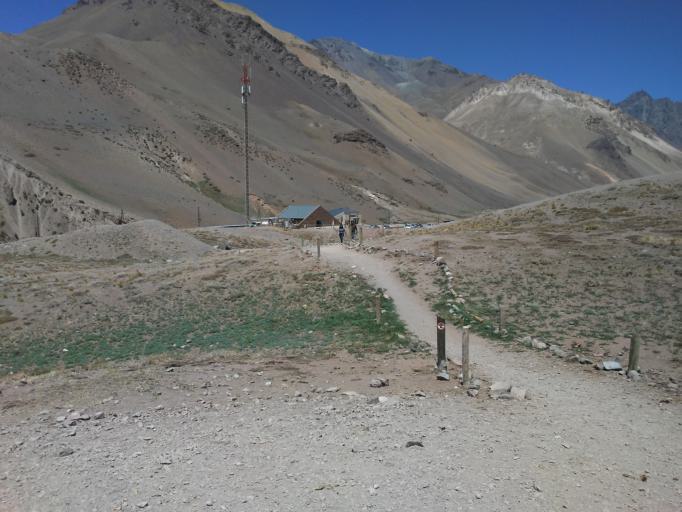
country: CL
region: Valparaiso
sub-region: Provincia de Los Andes
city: Los Andes
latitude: -32.8227
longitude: -69.9405
